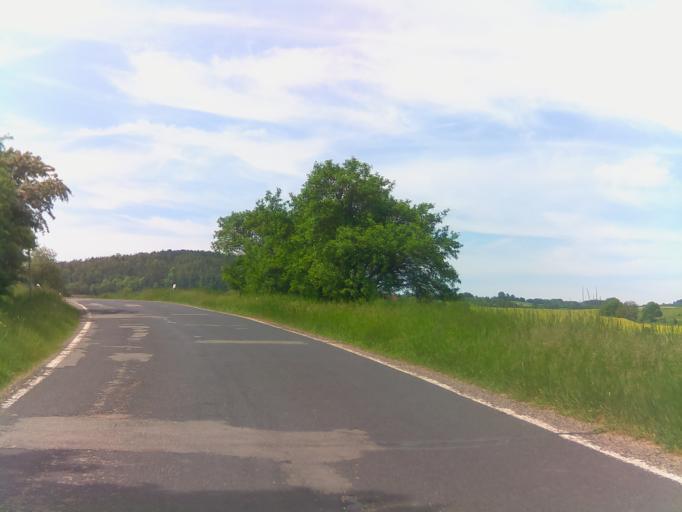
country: DE
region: Thuringia
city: Barchfeld
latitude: 50.7594
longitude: 11.1869
